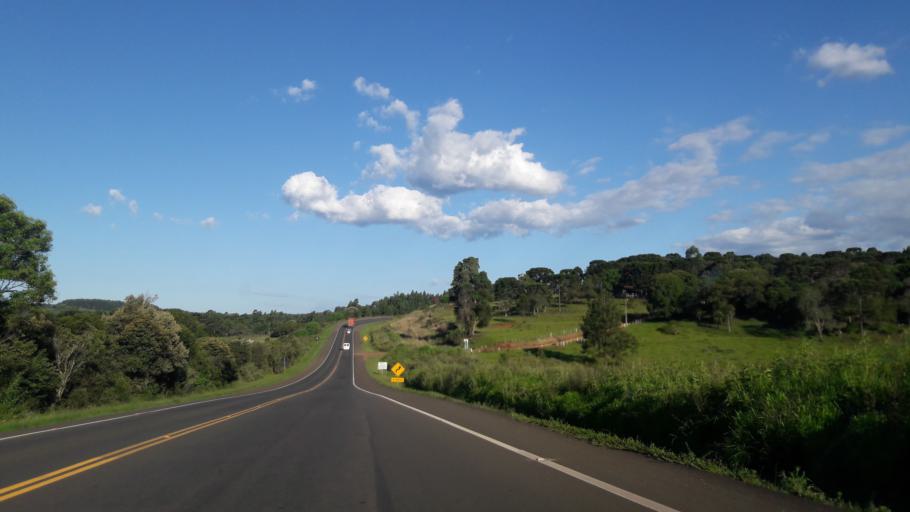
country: BR
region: Parana
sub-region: Guarapuava
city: Guarapuava
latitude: -25.3659
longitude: -51.3467
